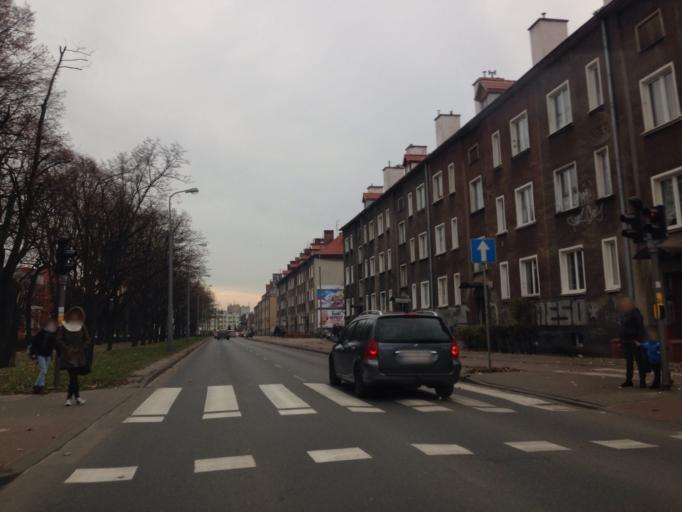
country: PL
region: Pomeranian Voivodeship
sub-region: Gdansk
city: Gdansk
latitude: 54.3854
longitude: 18.6121
